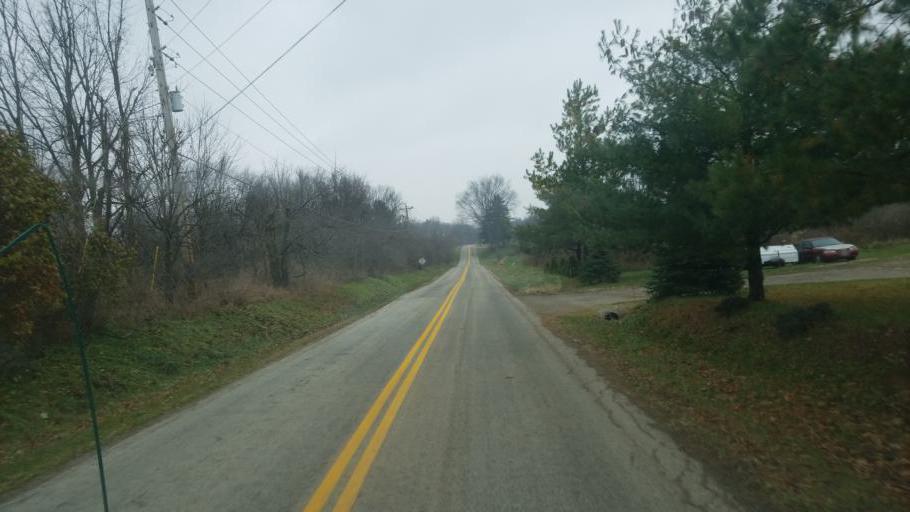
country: US
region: Ohio
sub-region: Huron County
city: New London
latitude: 41.0585
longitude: -82.3266
